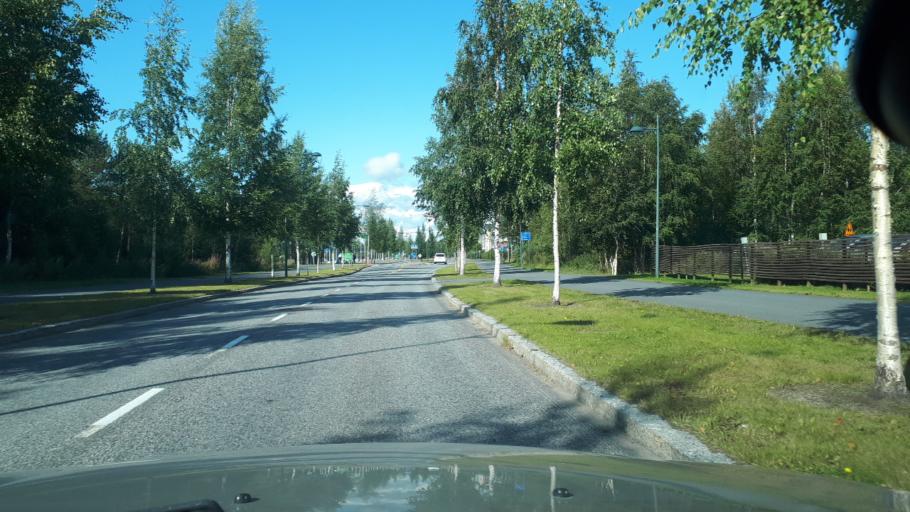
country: FI
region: Northern Ostrobothnia
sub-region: Oulu
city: Oulu
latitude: 65.0731
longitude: 25.4475
